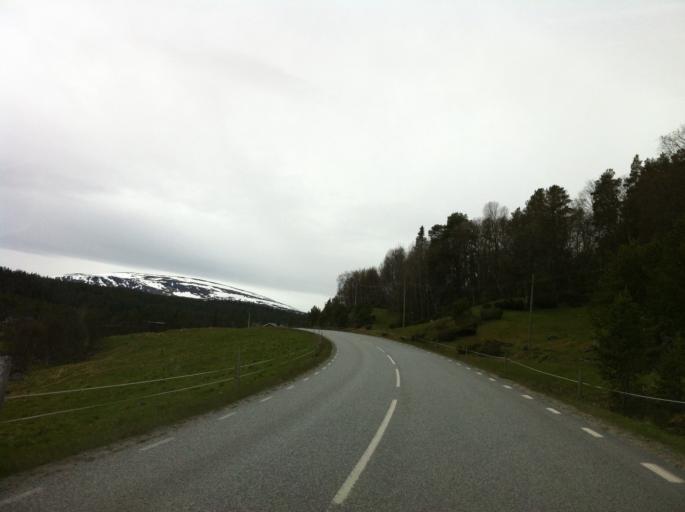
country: NO
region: Sor-Trondelag
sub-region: Tydal
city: Aas
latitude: 62.6170
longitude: 12.4825
